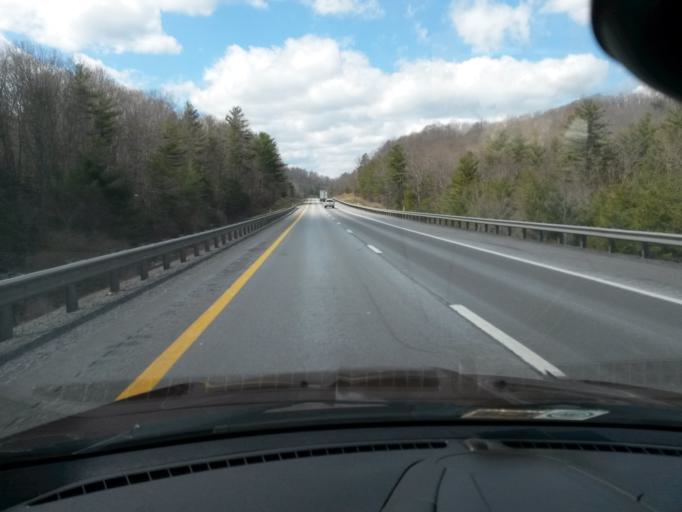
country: US
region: West Virginia
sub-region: Raleigh County
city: Daniels
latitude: 37.7033
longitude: -81.1430
